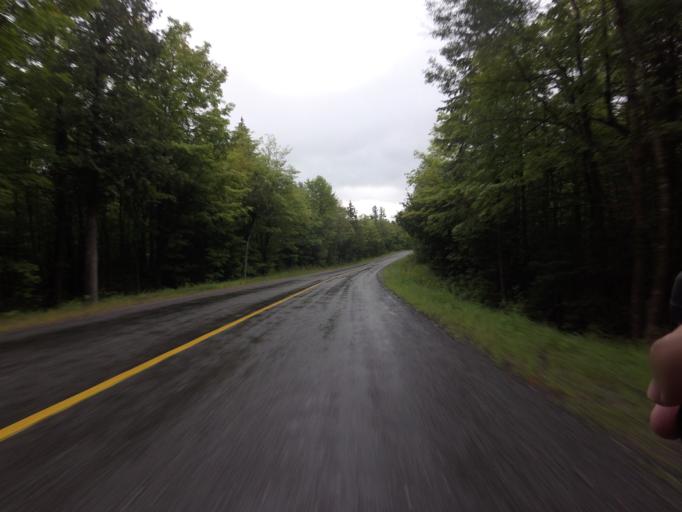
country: CA
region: Ontario
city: Renfrew
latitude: 45.0681
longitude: -76.6419
